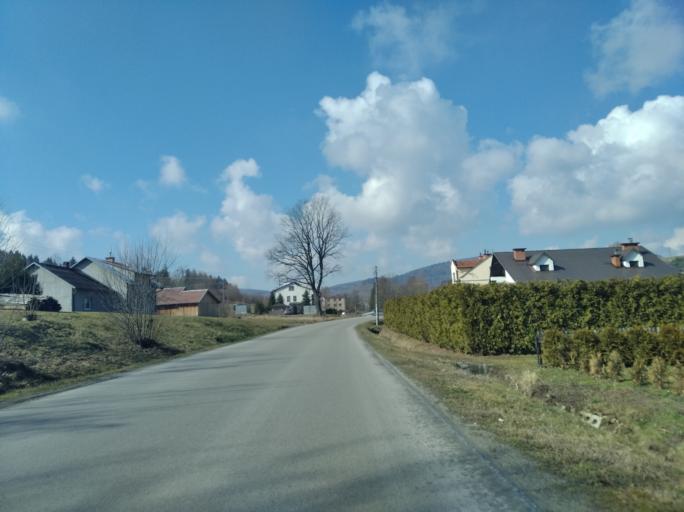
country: PL
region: Subcarpathian Voivodeship
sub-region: Powiat strzyzowski
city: Frysztak
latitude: 49.8711
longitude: 21.5969
